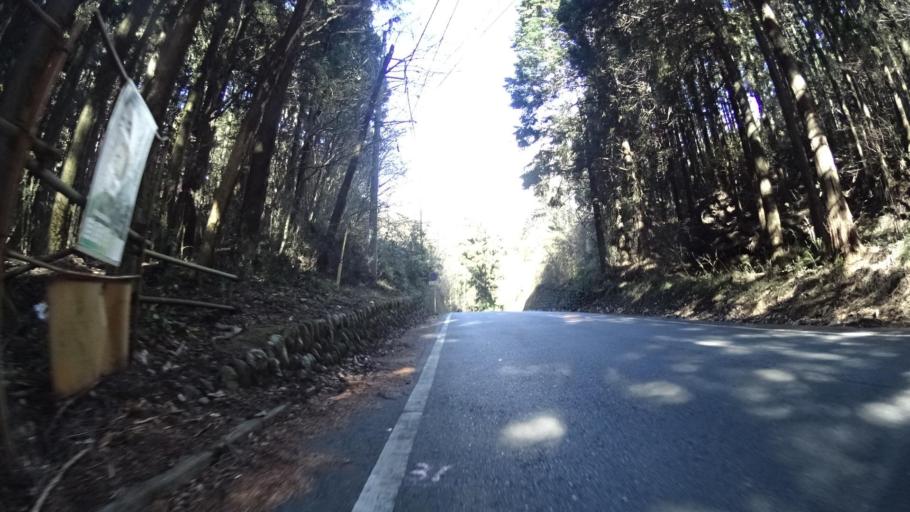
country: JP
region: Yamanashi
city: Uenohara
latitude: 35.5545
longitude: 139.2114
